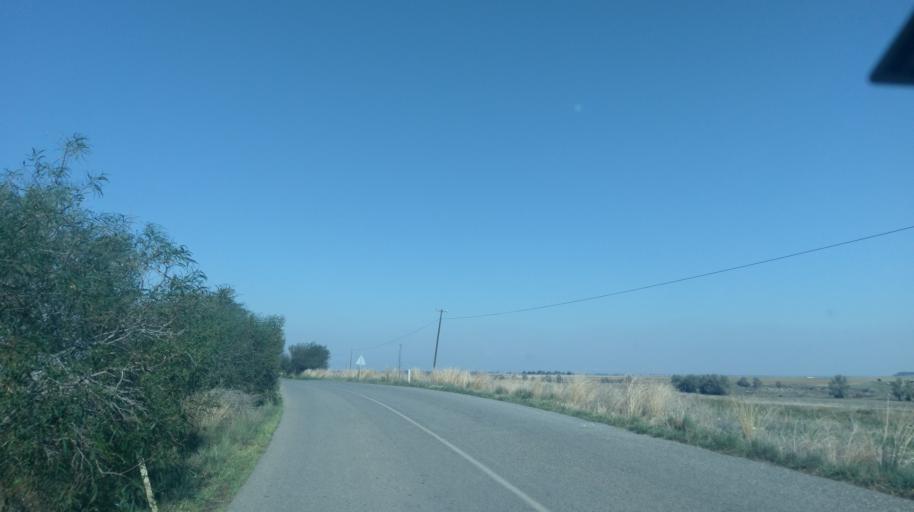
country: CY
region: Larnaka
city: Athienou
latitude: 35.1033
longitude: 33.4955
